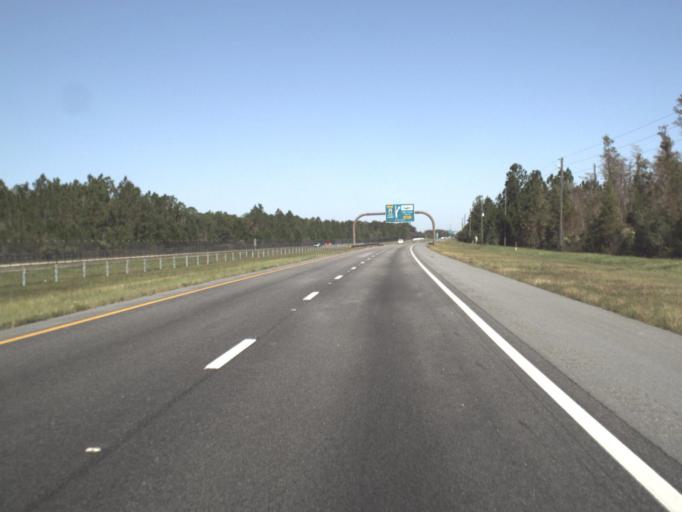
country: US
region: Florida
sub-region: Pasco County
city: Odessa
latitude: 28.2271
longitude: -82.5501
